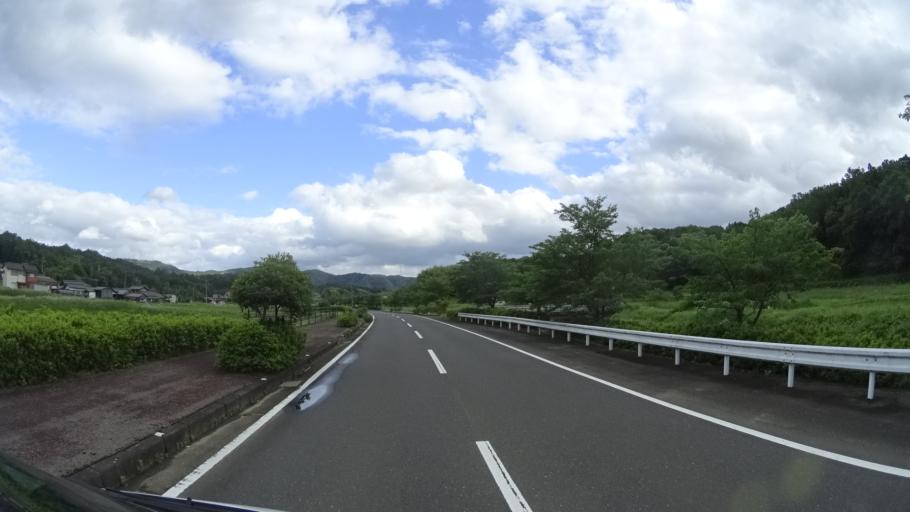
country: JP
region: Kyoto
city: Ayabe
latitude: 35.3415
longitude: 135.2903
